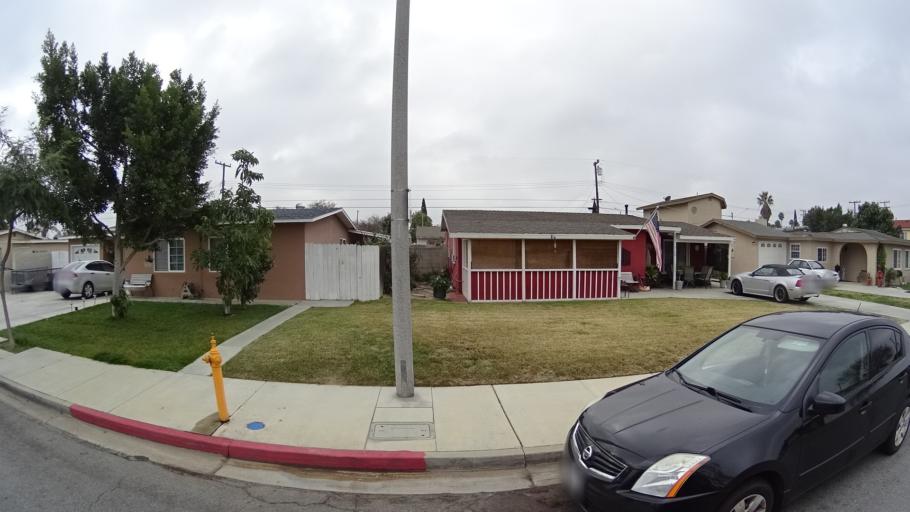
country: US
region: California
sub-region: Orange County
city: Stanton
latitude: 33.8338
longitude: -118.0014
